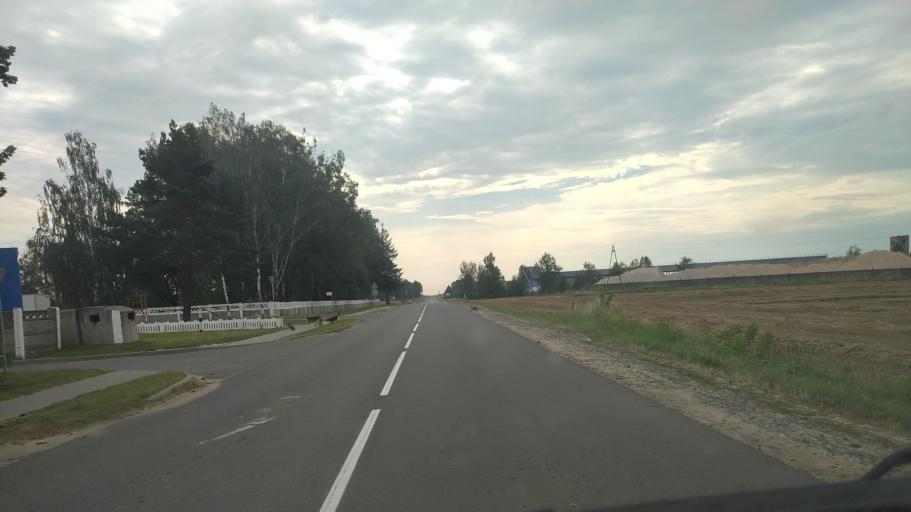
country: BY
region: Brest
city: Byaroza
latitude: 52.5540
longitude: 24.9268
